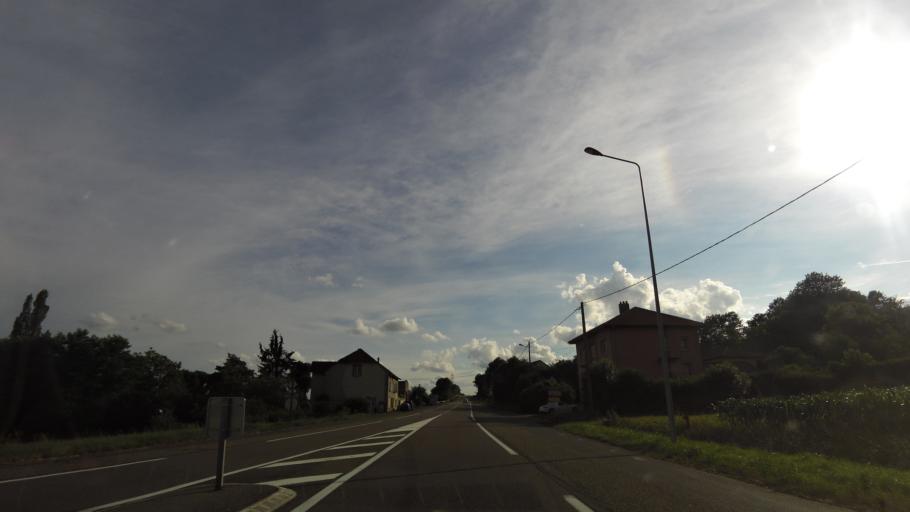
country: FR
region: Lorraine
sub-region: Departement de la Moselle
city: Sarrebourg
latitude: 48.7236
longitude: 7.0192
